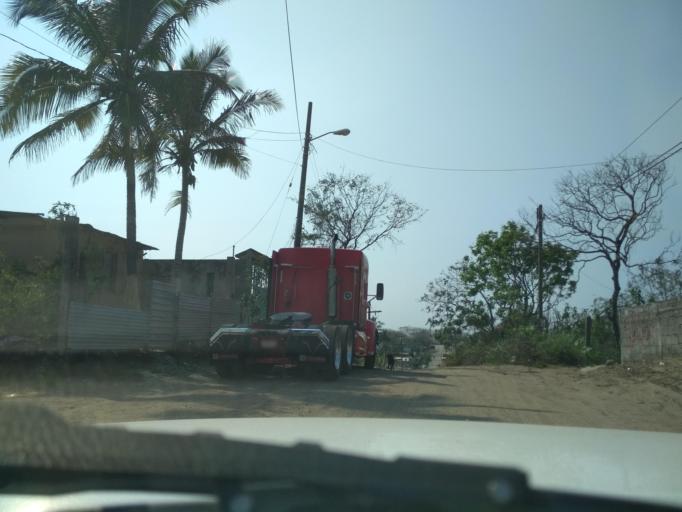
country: MX
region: Veracruz
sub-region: Veracruz
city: Colonia Chalchihuecan
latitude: 19.2134
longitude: -96.2122
